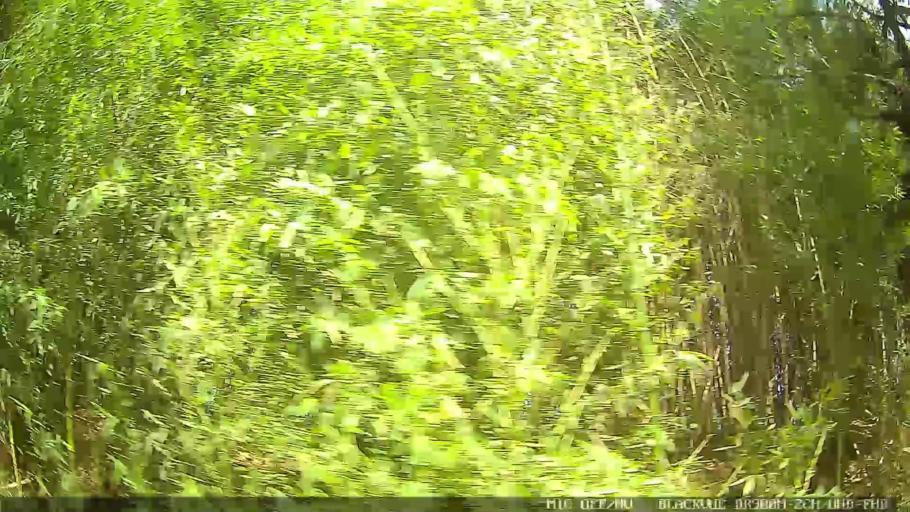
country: BR
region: Sao Paulo
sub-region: Artur Nogueira
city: Artur Nogueira
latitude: -22.5953
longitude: -47.0735
